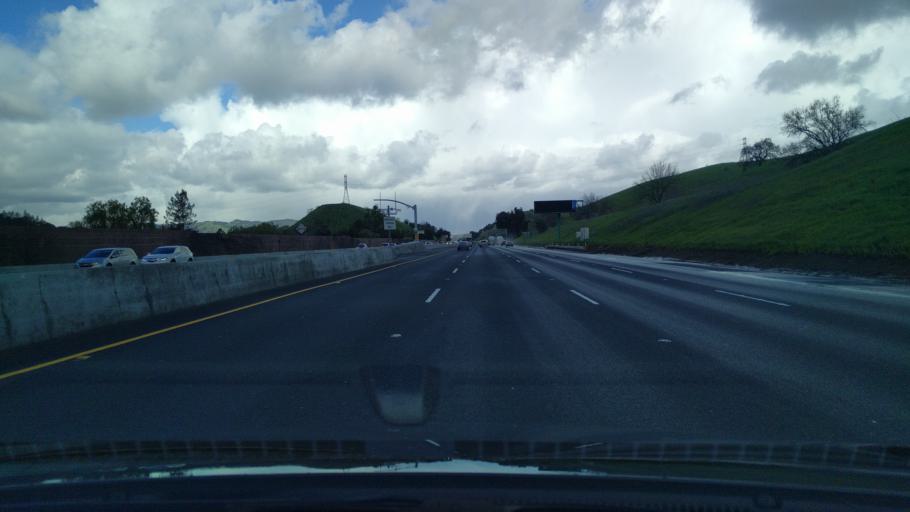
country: US
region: California
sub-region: Contra Costa County
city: Alamo
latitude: 37.8679
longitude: -122.0397
